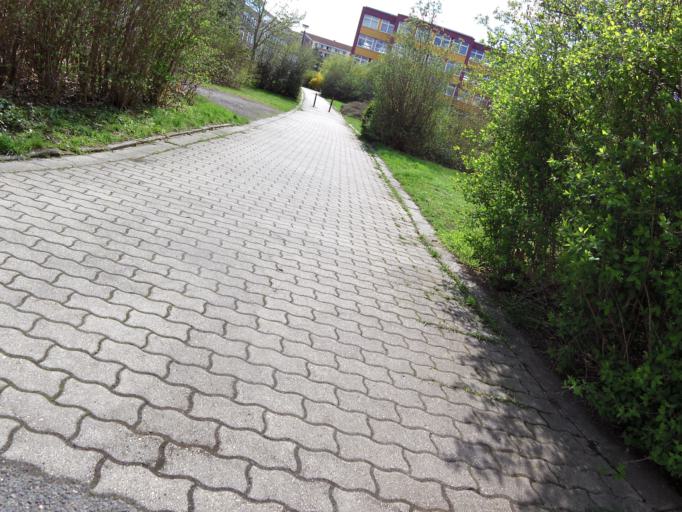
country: DE
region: Saxony
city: Markranstadt
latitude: 51.3276
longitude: 12.2884
